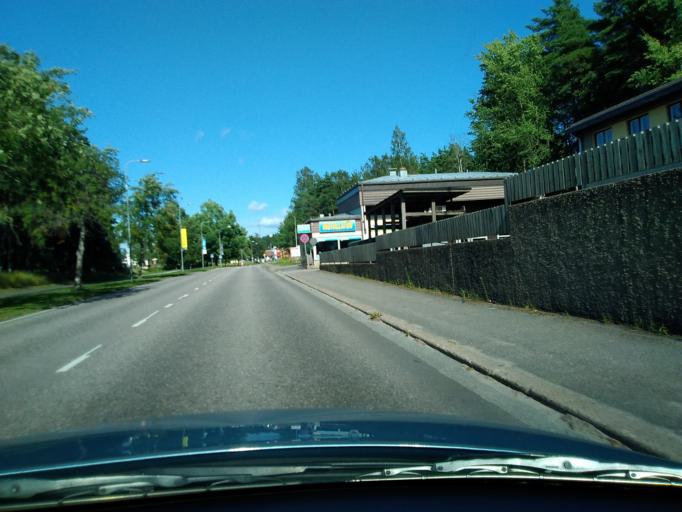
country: FI
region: Uusimaa
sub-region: Raaseporin
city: Ekenaes
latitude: 59.9799
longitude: 23.4513
